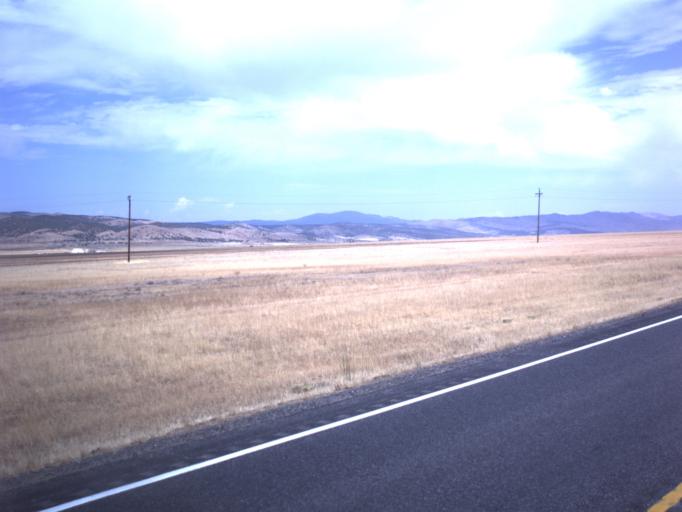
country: US
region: Utah
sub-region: Juab County
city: Nephi
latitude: 39.6052
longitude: -111.8617
